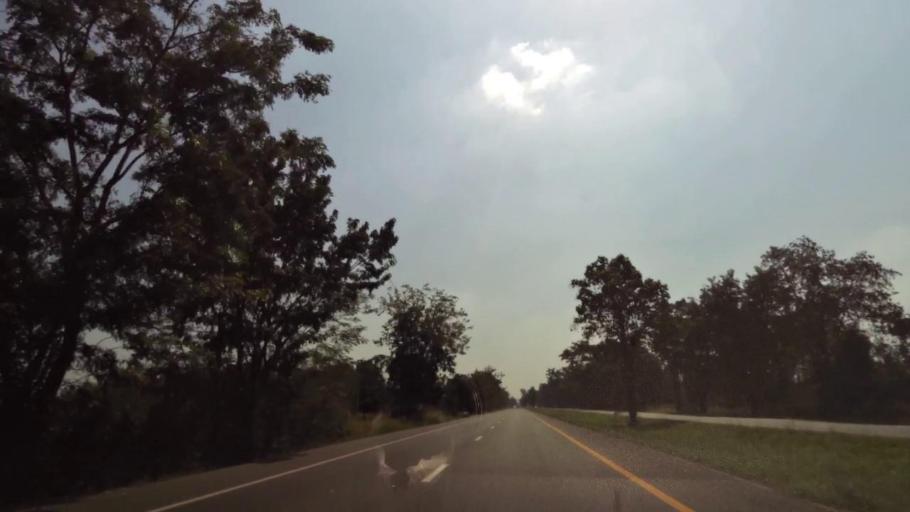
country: TH
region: Phichit
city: Bueng Na Rang
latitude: 16.2105
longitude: 100.1273
